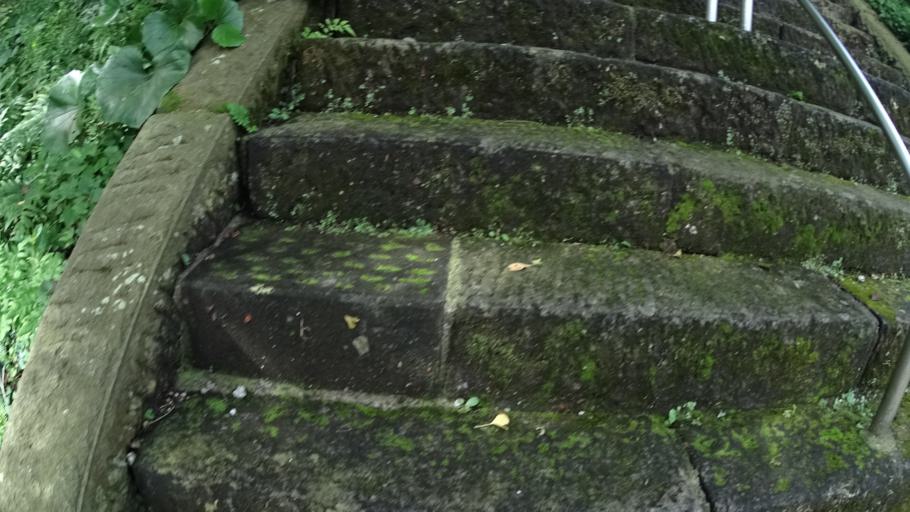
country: JP
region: Kanagawa
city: Yokosuka
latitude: 35.2793
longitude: 139.6412
